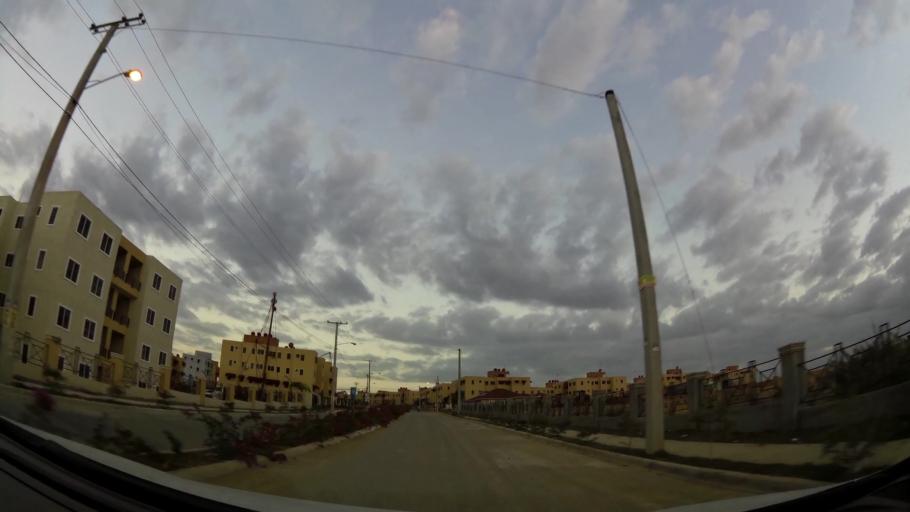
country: DO
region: Nacional
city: La Agustina
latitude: 18.5644
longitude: -69.9454
